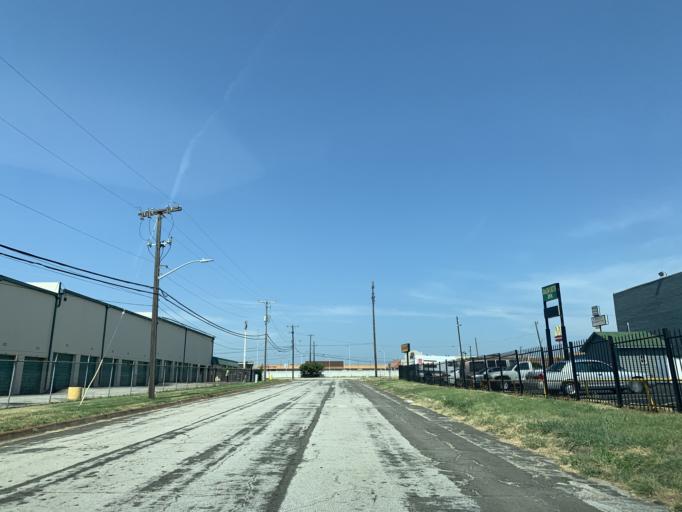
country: US
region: Texas
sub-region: Tarrant County
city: Edgecliff Village
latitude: 32.6750
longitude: -97.3188
